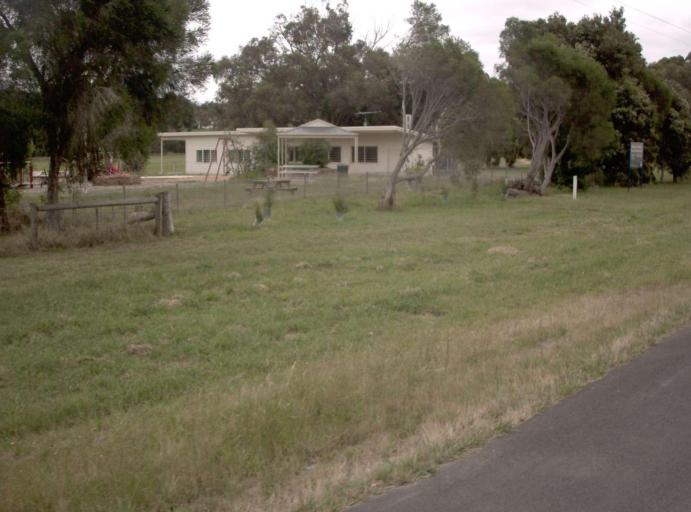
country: AU
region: Victoria
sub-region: Yarra Ranges
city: Yarra Glen
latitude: -37.6054
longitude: 145.4170
